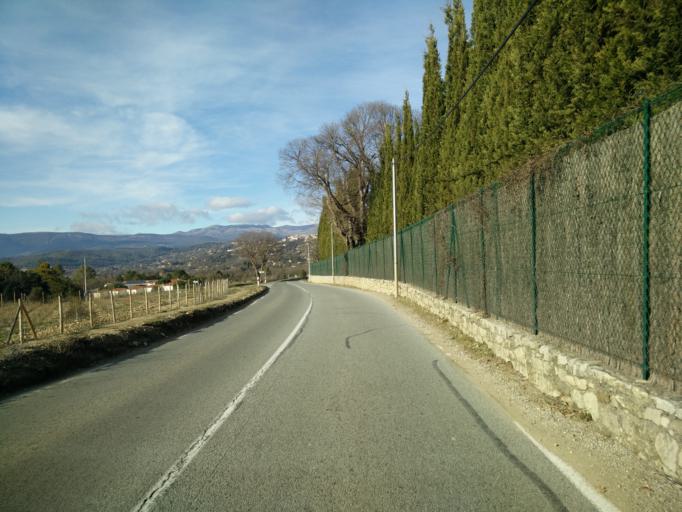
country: FR
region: Provence-Alpes-Cote d'Azur
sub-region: Departement du Var
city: Montauroux
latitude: 43.5962
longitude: 6.7880
